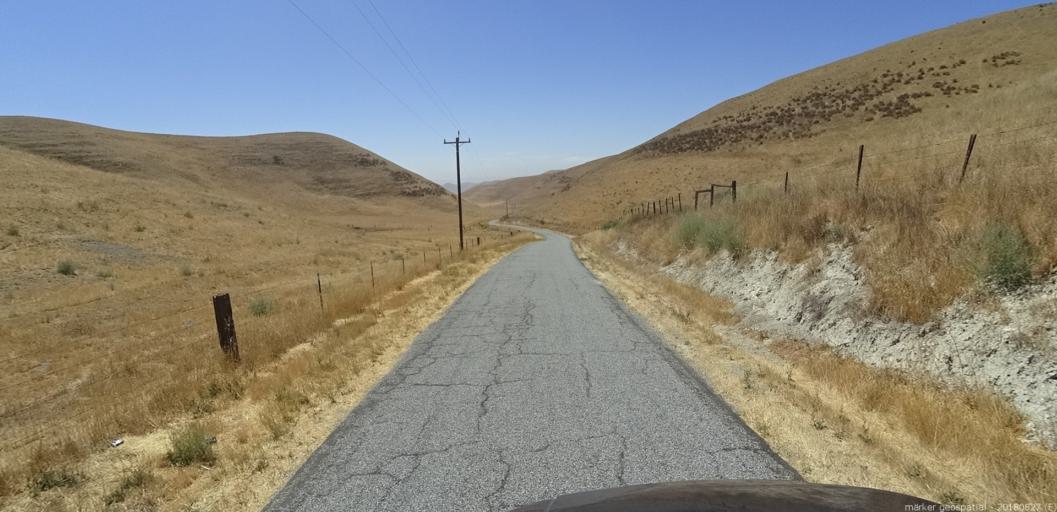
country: US
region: California
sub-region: Monterey County
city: King City
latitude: 36.1566
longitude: -120.8648
